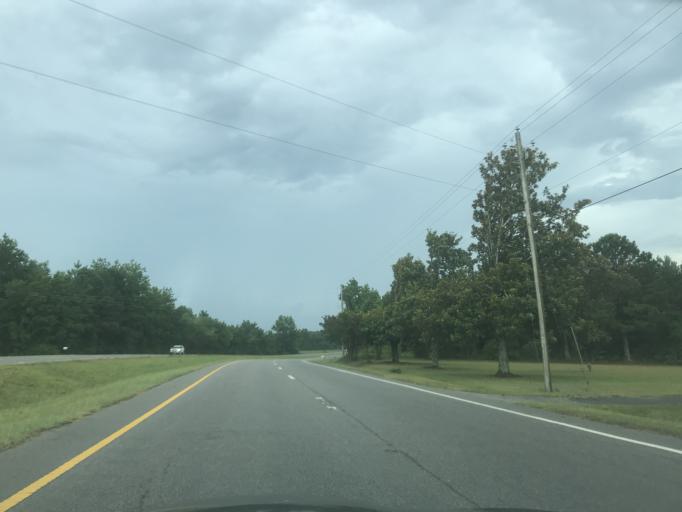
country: US
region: North Carolina
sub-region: Johnston County
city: Wilsons Mills
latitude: 35.5717
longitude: -78.3950
